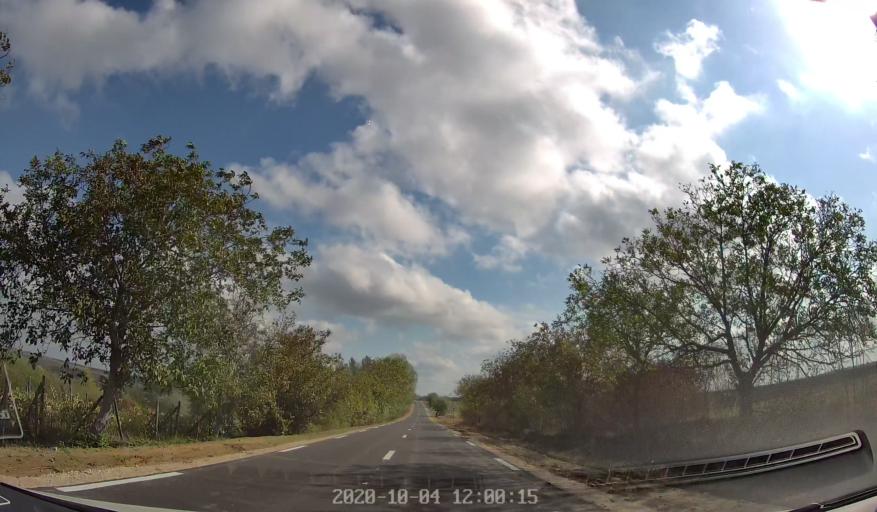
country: MD
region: Rezina
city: Saharna
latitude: 47.6314
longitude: 28.8680
